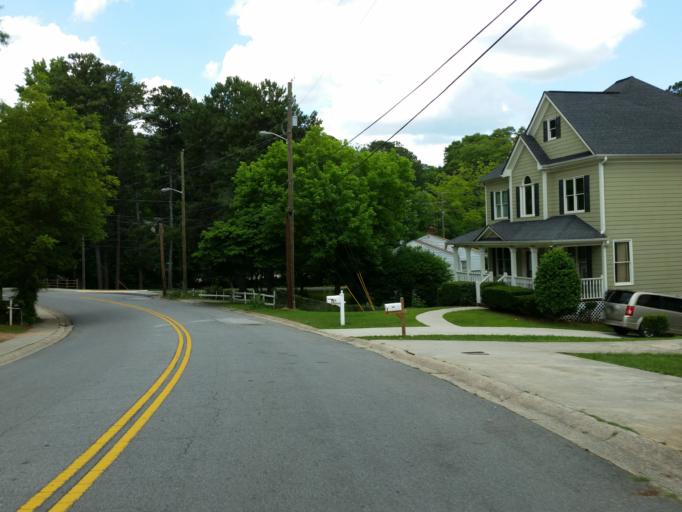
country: US
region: Georgia
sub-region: Cobb County
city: Marietta
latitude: 33.9464
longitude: -84.5301
